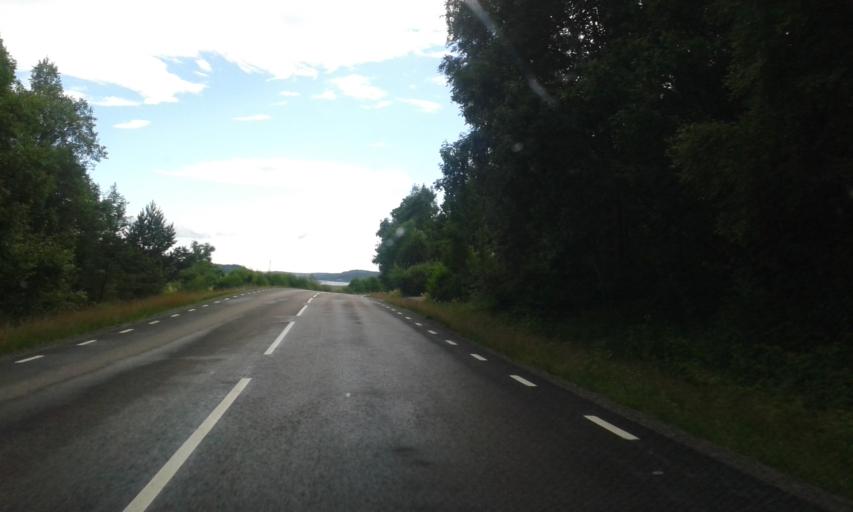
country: SE
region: Vaestra Goetaland
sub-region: Ale Kommun
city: Alvangen
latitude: 57.9624
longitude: 12.0987
